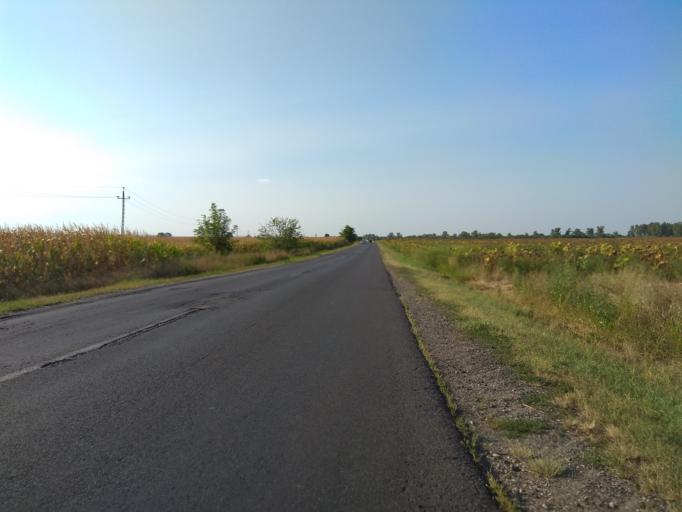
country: HU
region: Borsod-Abauj-Zemplen
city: Onod
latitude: 48.0163
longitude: 20.9067
